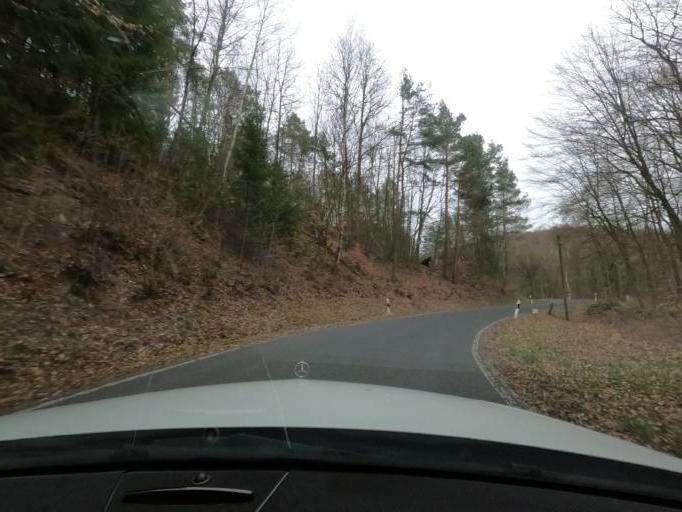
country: DE
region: Thuringia
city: Kella
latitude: 51.2195
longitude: 10.0765
